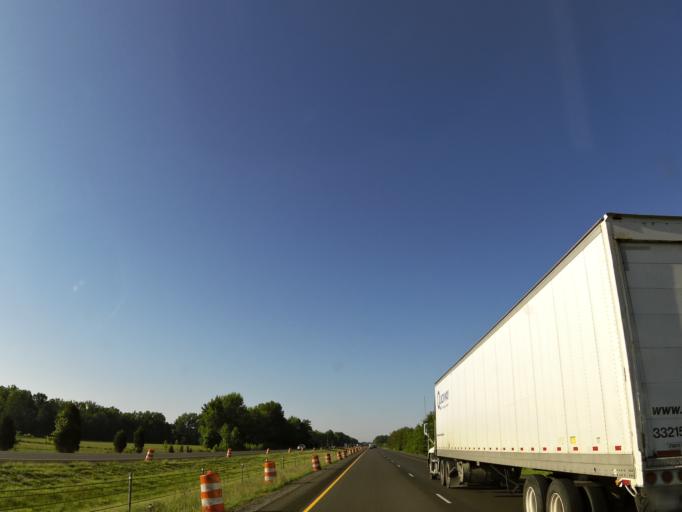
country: US
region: Indiana
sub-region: Jackson County
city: Crothersville
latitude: 38.8786
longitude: -85.8104
